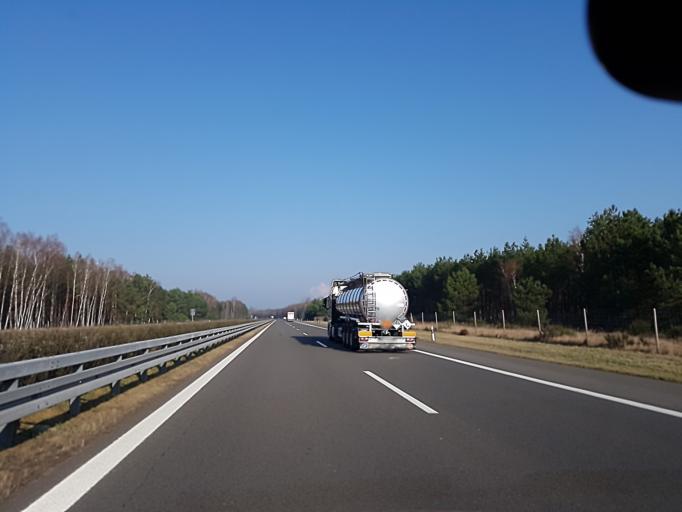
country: DE
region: Brandenburg
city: Forst
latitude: 51.6945
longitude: 14.6657
